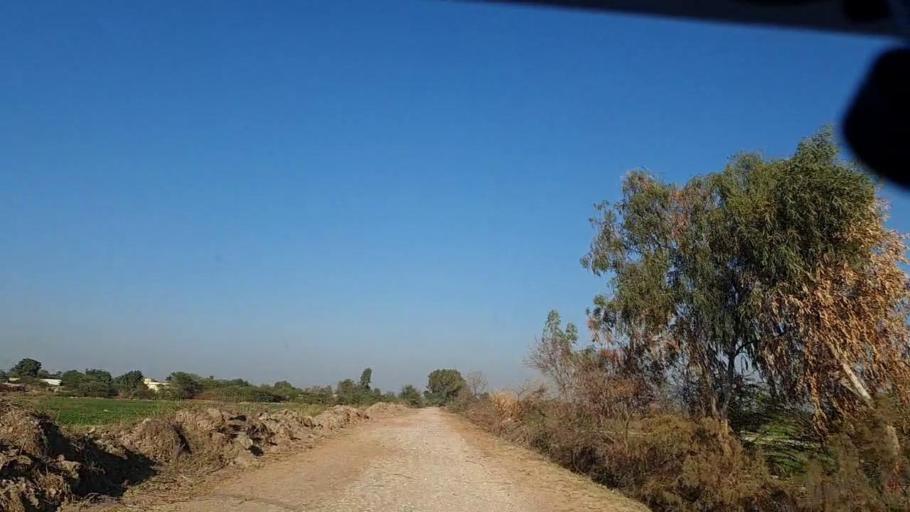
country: PK
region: Sindh
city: Khanpur
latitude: 27.7587
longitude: 69.3359
